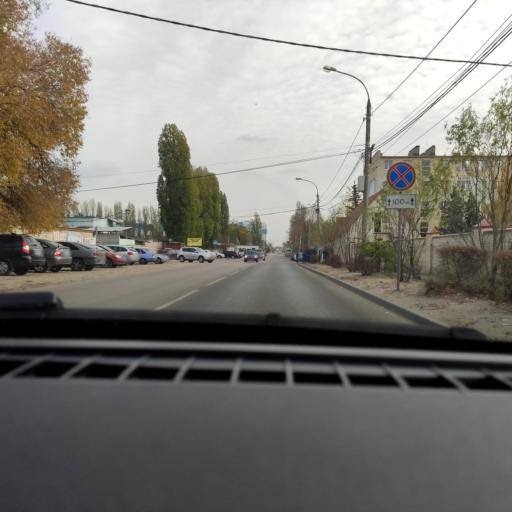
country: RU
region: Voronezj
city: Maslovka
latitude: 51.6364
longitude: 39.2814
